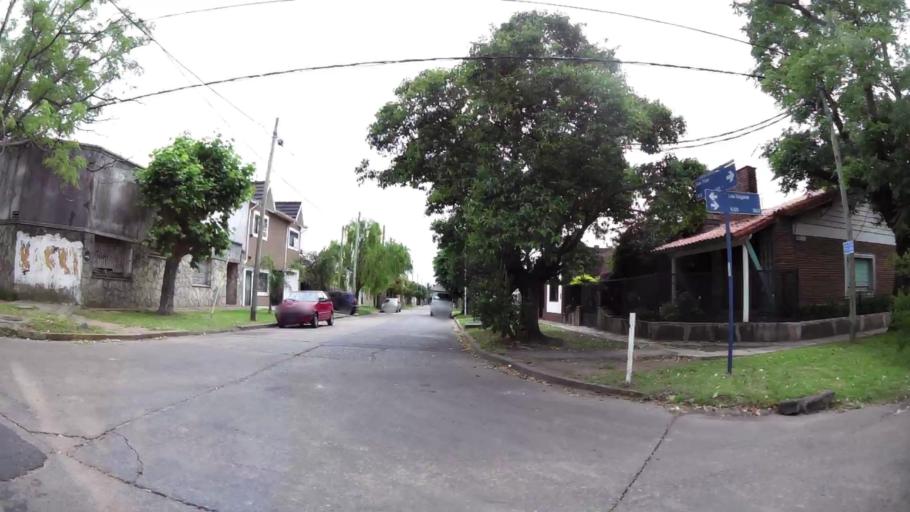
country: AR
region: Buenos Aires F.D.
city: Villa Lugano
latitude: -34.7031
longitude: -58.5101
